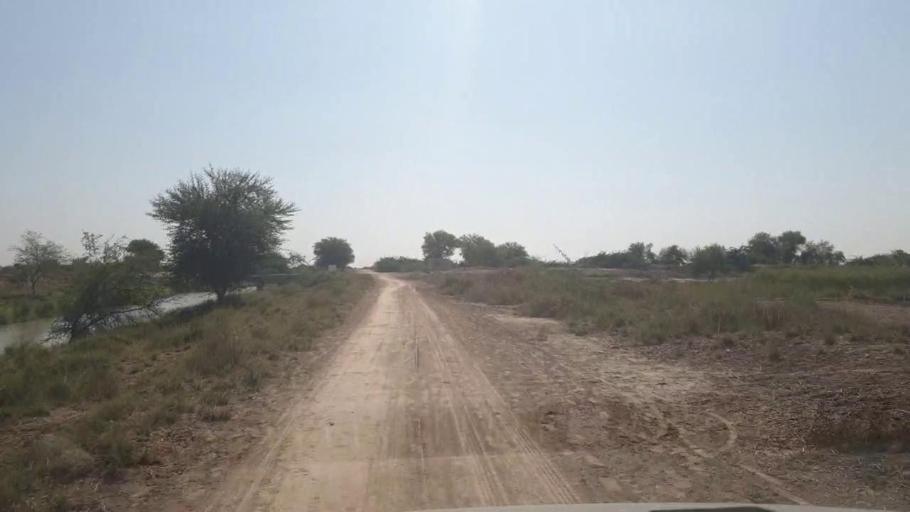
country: PK
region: Sindh
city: Tando Bago
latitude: 24.8881
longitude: 69.1645
